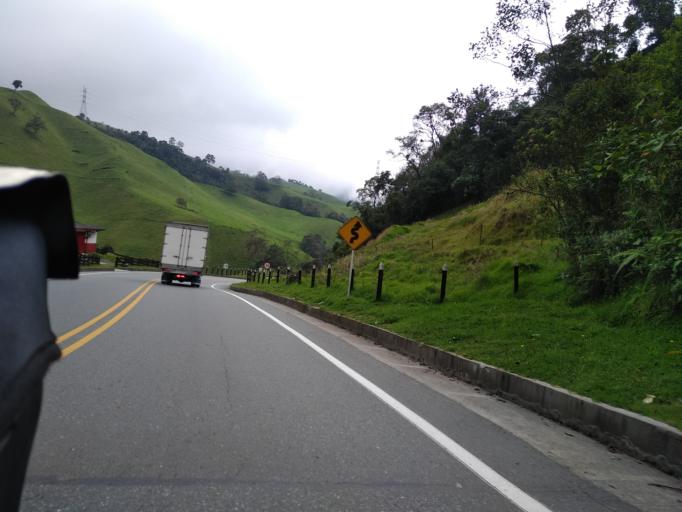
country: CO
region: Caldas
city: Villamaria
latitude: 5.0329
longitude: -75.3785
